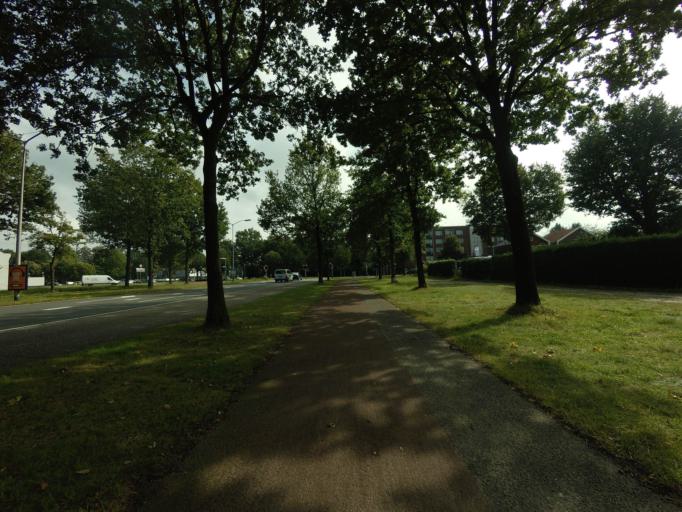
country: NL
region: Overijssel
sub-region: Gemeente Hengelo
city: Hengelo
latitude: 52.2761
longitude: 6.8226
